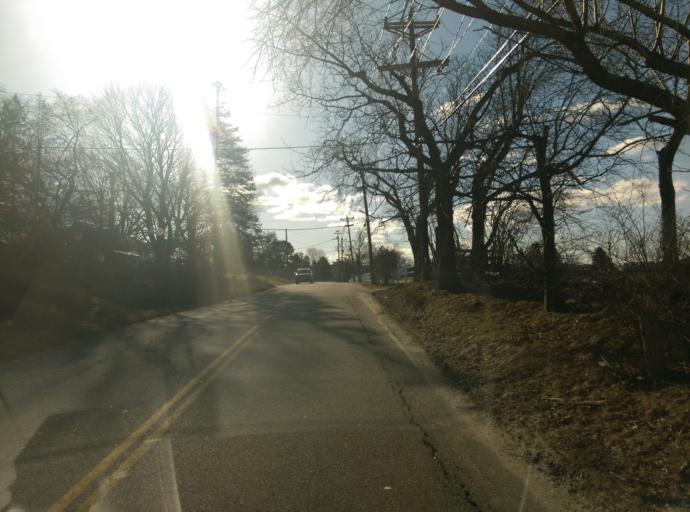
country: US
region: Massachusetts
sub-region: Essex County
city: Haverhill
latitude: 42.7553
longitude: -71.1203
